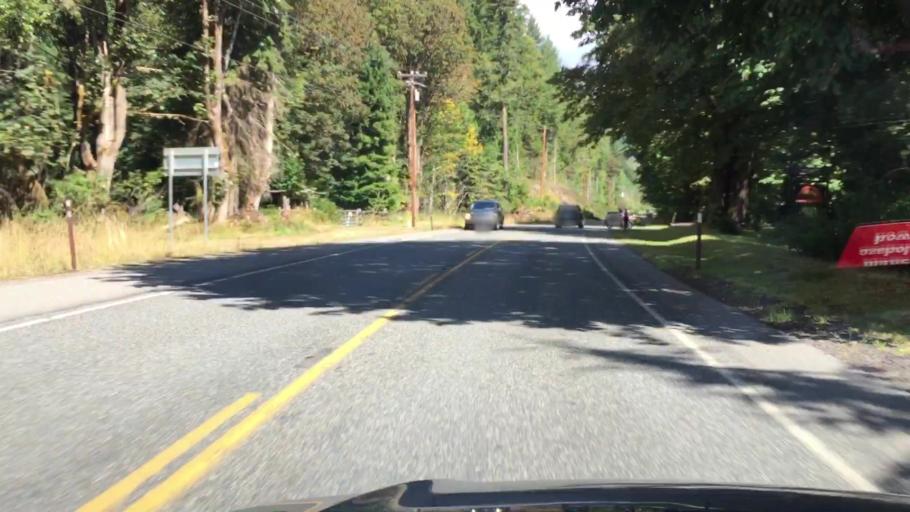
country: US
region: Washington
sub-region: Pierce County
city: Eatonville
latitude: 46.7585
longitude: -122.0497
